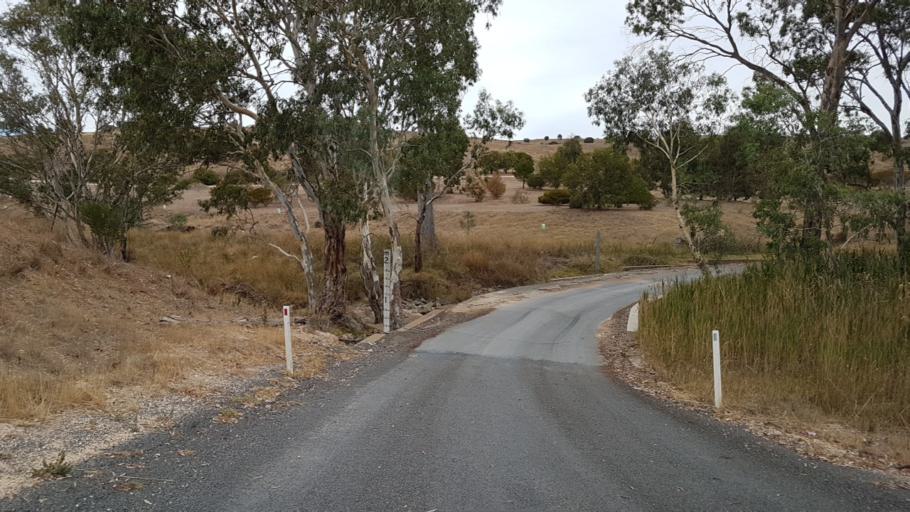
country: AU
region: South Australia
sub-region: Mount Barker
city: Callington
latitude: -35.0066
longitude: 139.0334
